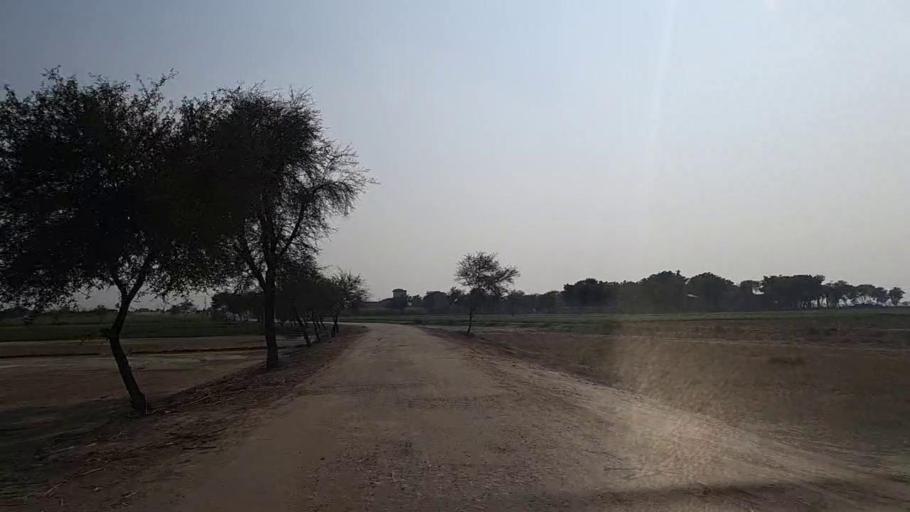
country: PK
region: Sindh
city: Daur
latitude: 26.4014
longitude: 68.4175
